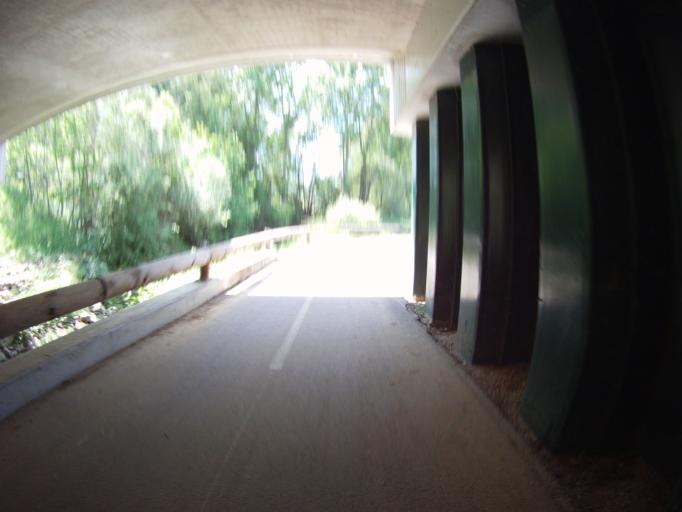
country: FR
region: Lorraine
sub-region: Departement de Meurthe-et-Moselle
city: Eulmont
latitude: 48.7411
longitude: 6.2223
